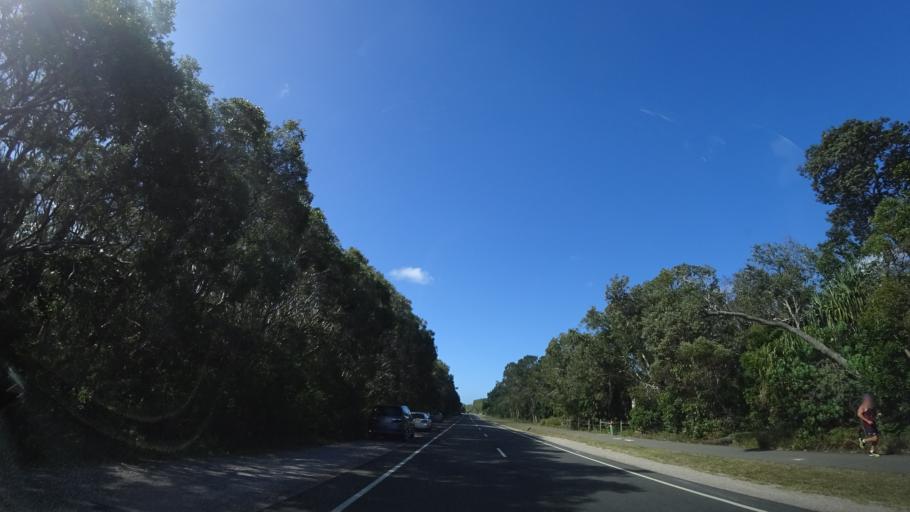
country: AU
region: Queensland
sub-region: Sunshine Coast
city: Mooloolaba
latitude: -26.6223
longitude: 153.1004
